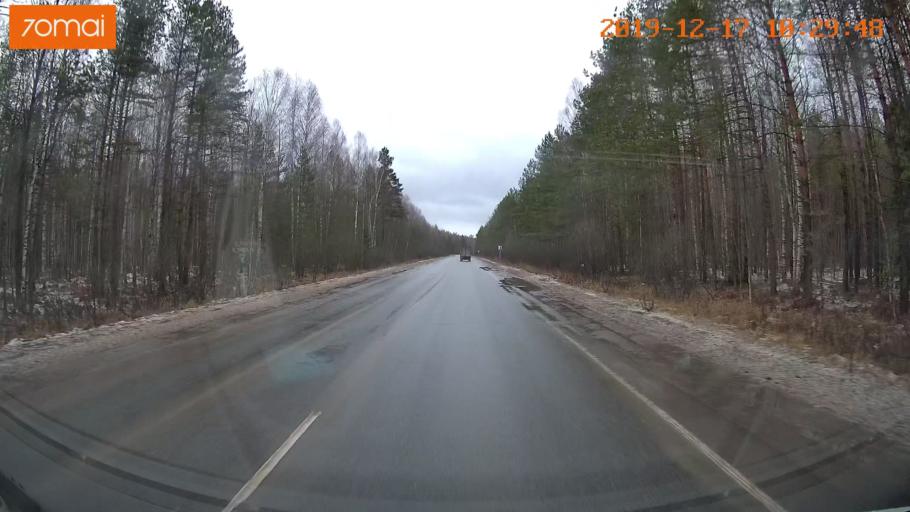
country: RU
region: Vladimir
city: Anopino
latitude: 55.6483
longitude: 40.7162
